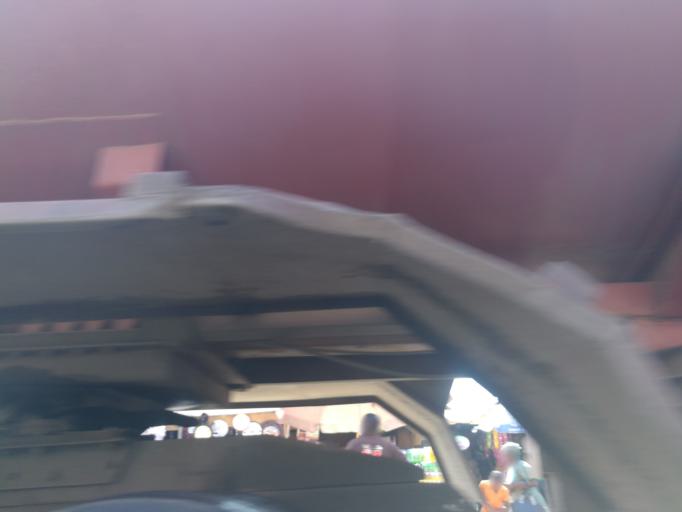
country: NG
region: Lagos
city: Agege
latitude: 6.6238
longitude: 3.3249
